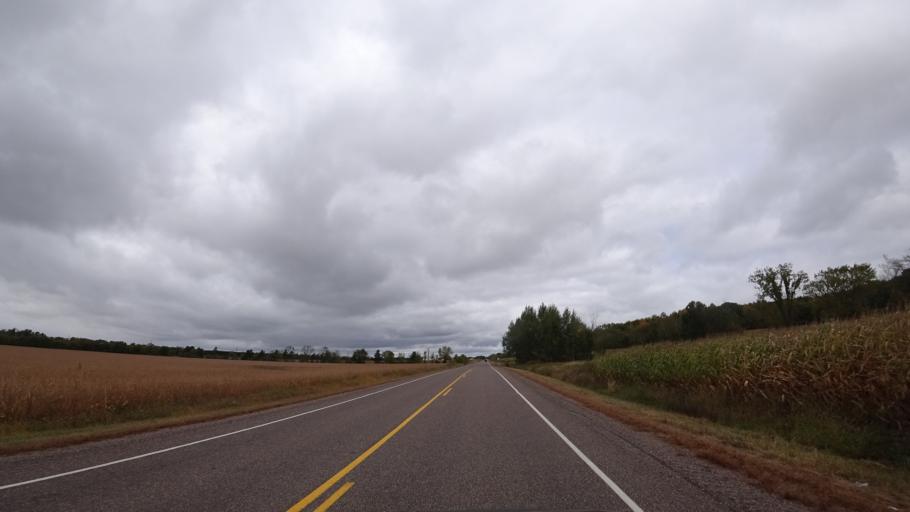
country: US
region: Wisconsin
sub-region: Chippewa County
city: Lake Wissota
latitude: 44.9984
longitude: -91.2867
